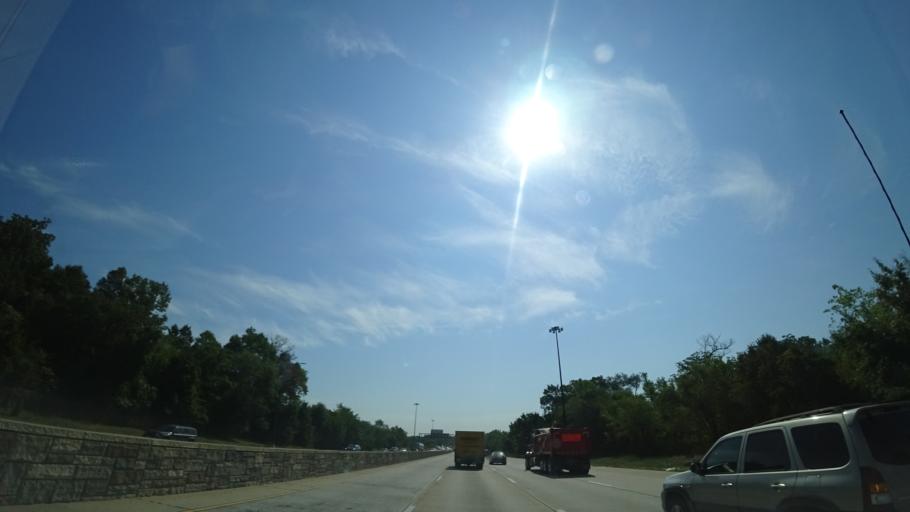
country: US
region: Maryland
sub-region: Prince George's County
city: Colmar Manor
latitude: 38.9187
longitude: -76.9467
